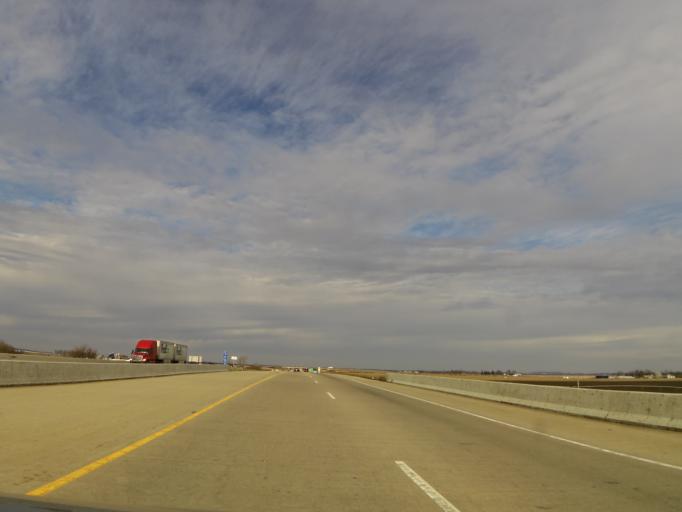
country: US
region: Wisconsin
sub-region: Rock County
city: Janesville
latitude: 42.6225
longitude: -88.9824
